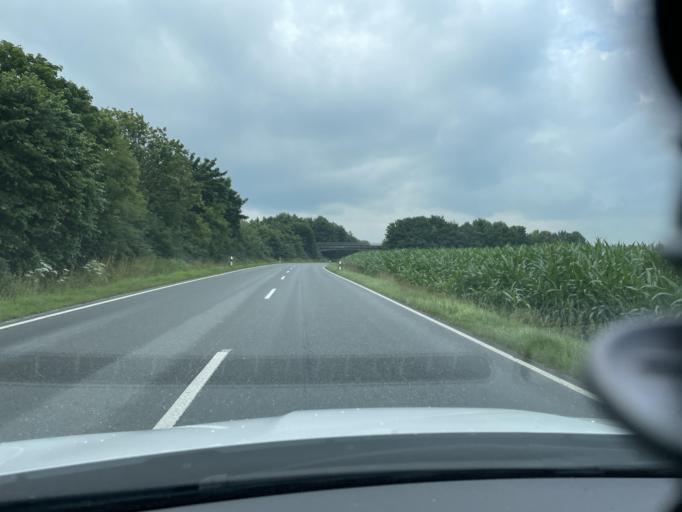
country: DE
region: Bavaria
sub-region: Upper Bavaria
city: Schechen
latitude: 47.9398
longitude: 12.1339
